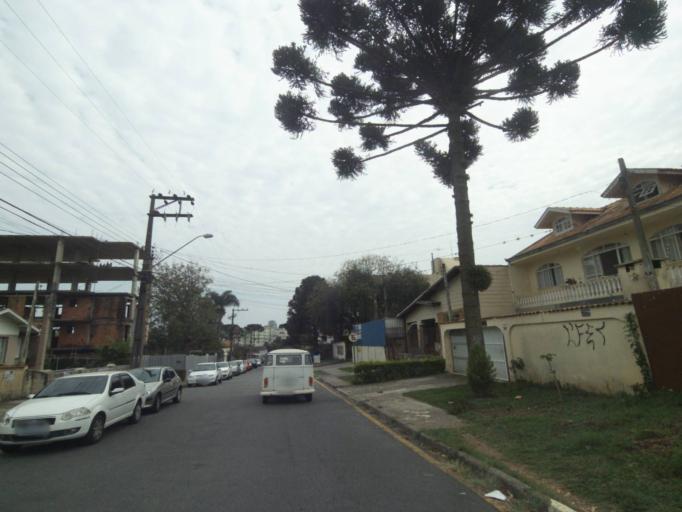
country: BR
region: Parana
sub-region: Curitiba
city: Curitiba
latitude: -25.4524
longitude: -49.3019
